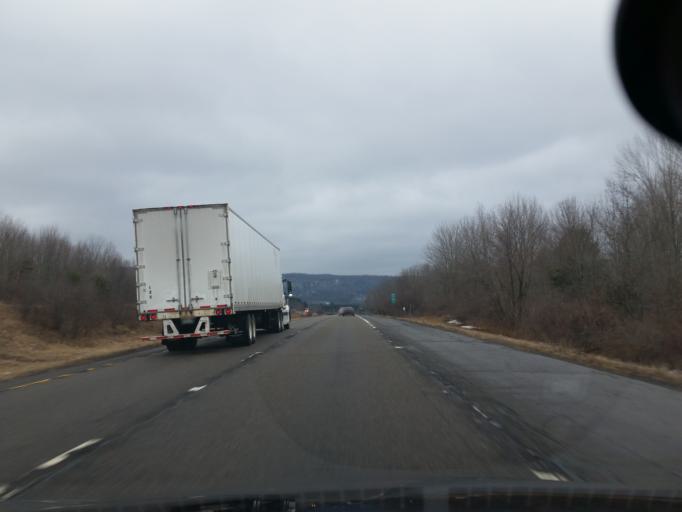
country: US
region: New York
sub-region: Broome County
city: Chenango Bridge
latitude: 42.0850
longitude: -75.8090
